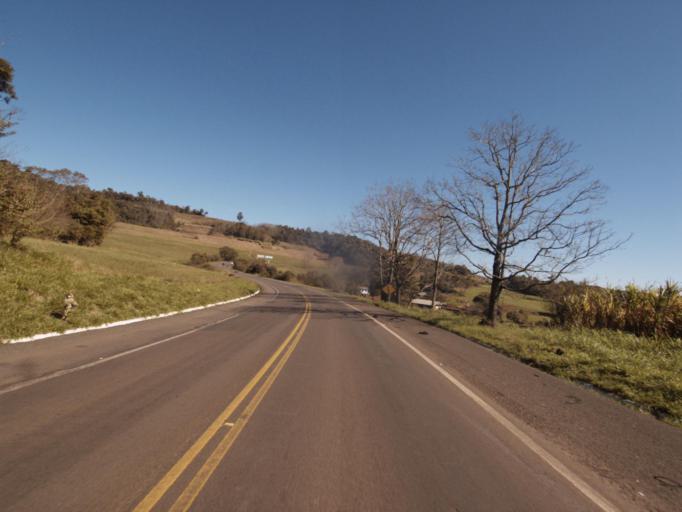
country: BR
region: Rio Grande do Sul
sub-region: Frederico Westphalen
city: Frederico Westphalen
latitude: -26.7974
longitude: -53.3264
